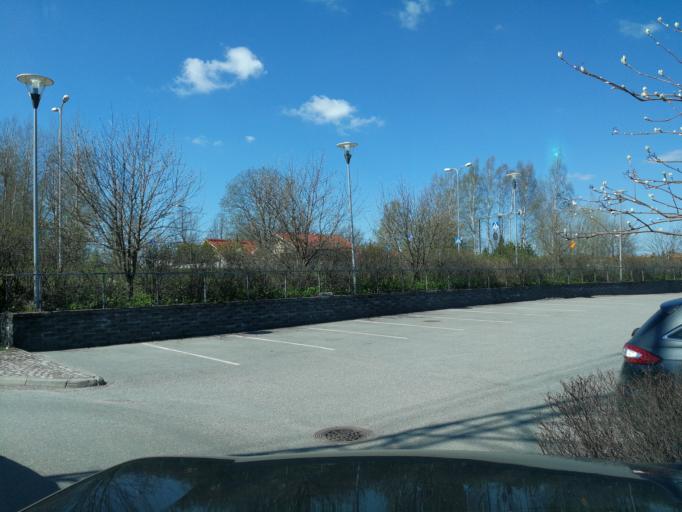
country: FI
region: Uusimaa
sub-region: Helsinki
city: Vantaa
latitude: 60.2775
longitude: 24.9720
